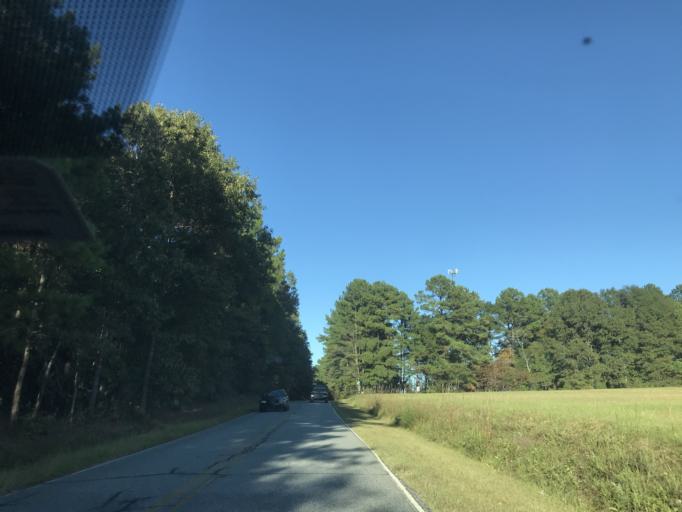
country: US
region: South Carolina
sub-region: Spartanburg County
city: Mayo
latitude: 35.0970
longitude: -81.8525
